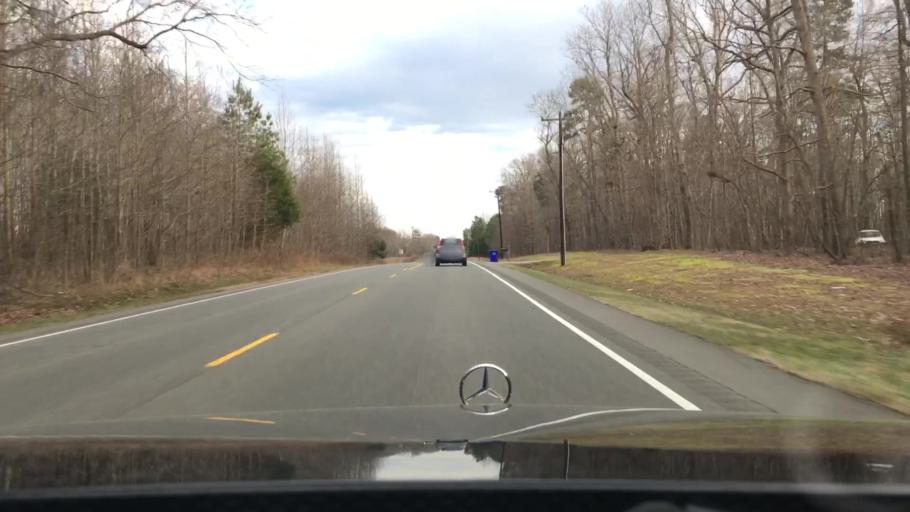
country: US
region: North Carolina
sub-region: Alamance County
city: Mebane
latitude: 36.2122
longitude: -79.1687
